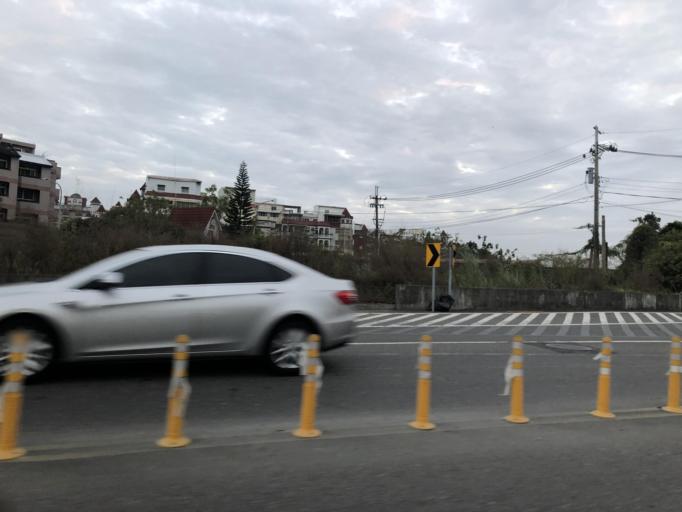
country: TW
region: Taiwan
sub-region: Tainan
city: Tainan
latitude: 23.0226
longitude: 120.3003
